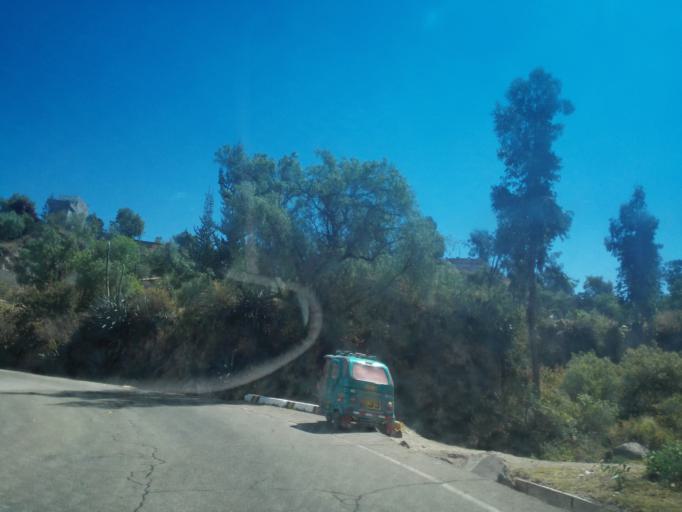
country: PE
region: Ayacucho
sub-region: Provincia de Huamanga
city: Ayacucho
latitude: -13.1645
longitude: -74.2425
